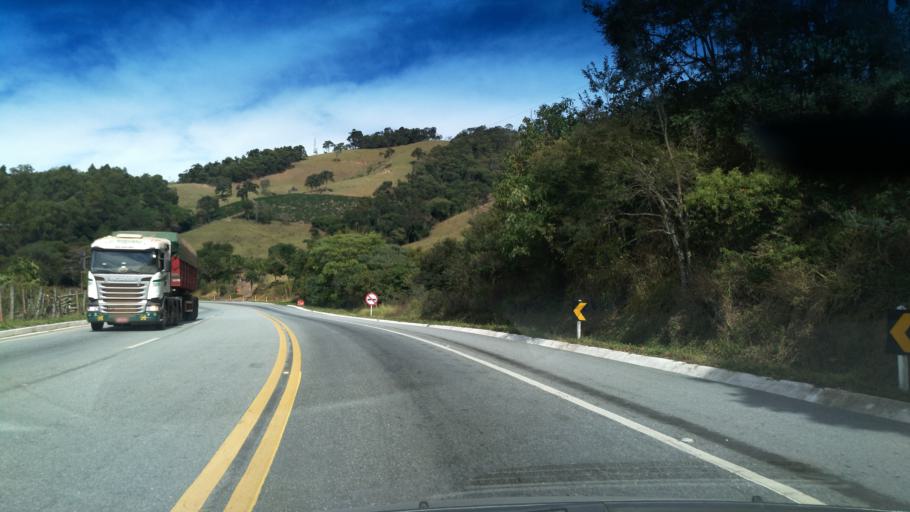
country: BR
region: Minas Gerais
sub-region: Borda Da Mata
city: Borda da Mata
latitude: -22.1317
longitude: -46.1494
